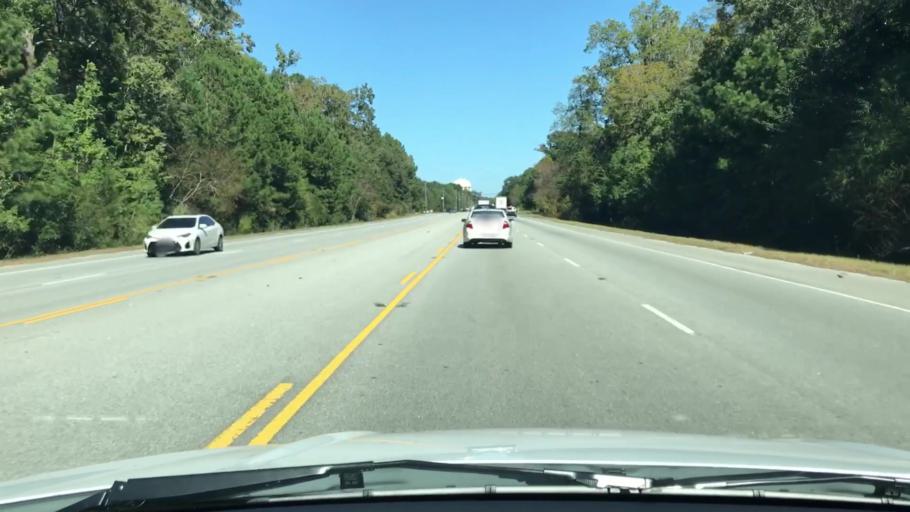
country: US
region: South Carolina
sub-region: Beaufort County
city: Shell Point
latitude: 32.4058
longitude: -80.7567
